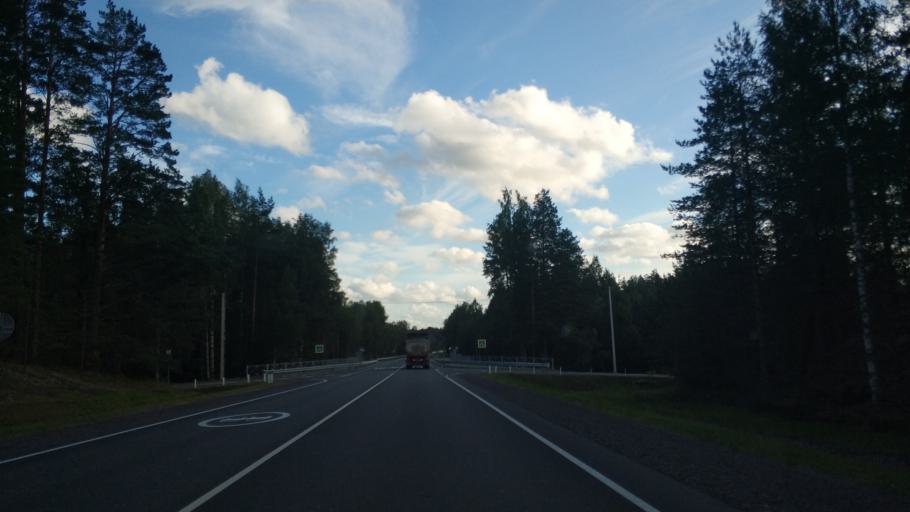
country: RU
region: Leningrad
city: Priozersk
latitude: 60.8670
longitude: 30.1599
